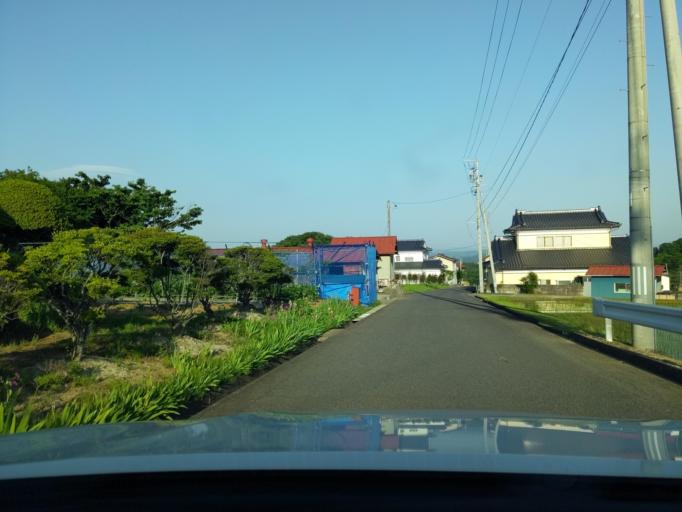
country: JP
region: Fukushima
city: Motomiya
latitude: 37.5382
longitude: 140.3486
